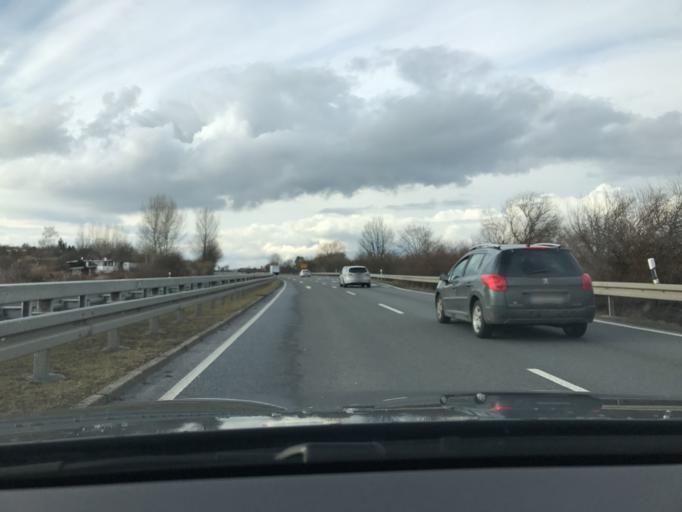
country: DE
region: Saxony-Anhalt
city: Roblingen am See
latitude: 51.4827
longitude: 11.7053
